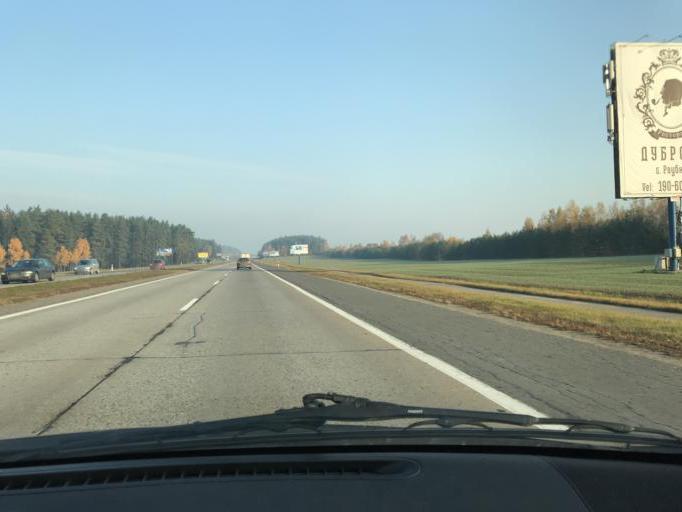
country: BY
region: Minsk
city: Borovlyany
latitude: 53.9936
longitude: 27.6572
